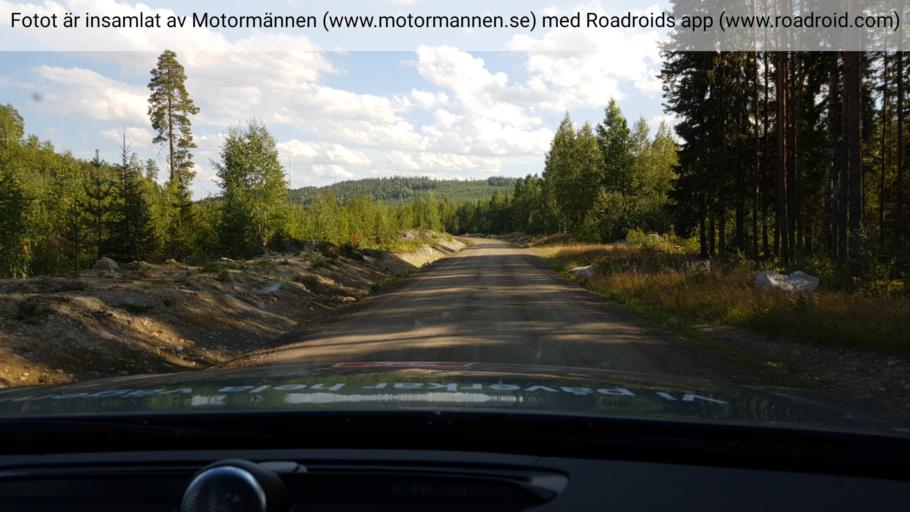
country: SE
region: Jaemtland
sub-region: Stroemsunds Kommun
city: Stroemsund
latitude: 63.9878
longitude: 16.0076
